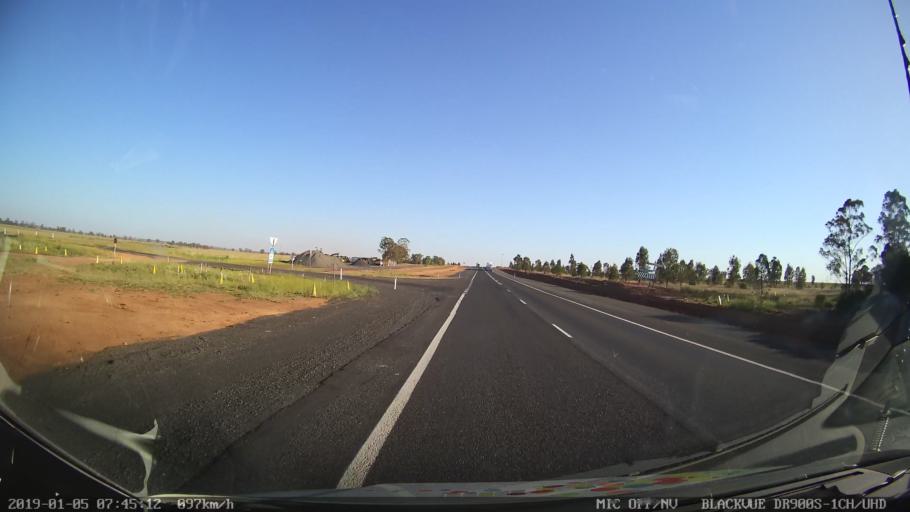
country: AU
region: New South Wales
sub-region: Gilgandra
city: Gilgandra
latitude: -31.8615
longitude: 148.6417
